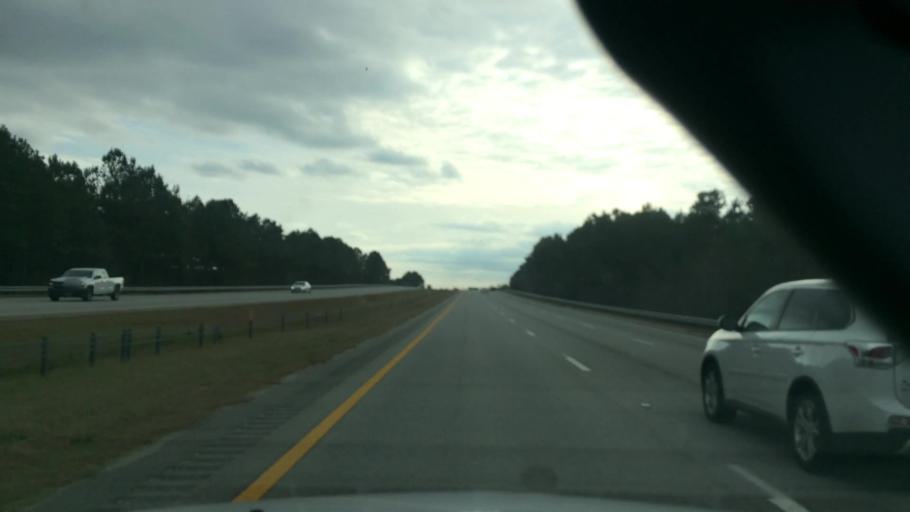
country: US
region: South Carolina
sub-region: Horry County
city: North Myrtle Beach
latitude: 33.8561
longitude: -78.6971
